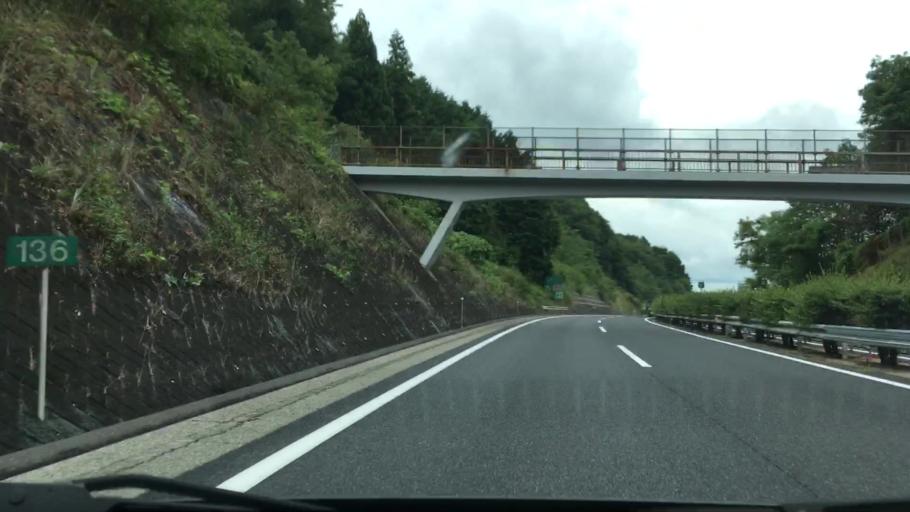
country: JP
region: Okayama
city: Tsuyama
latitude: 35.0205
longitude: 134.2000
